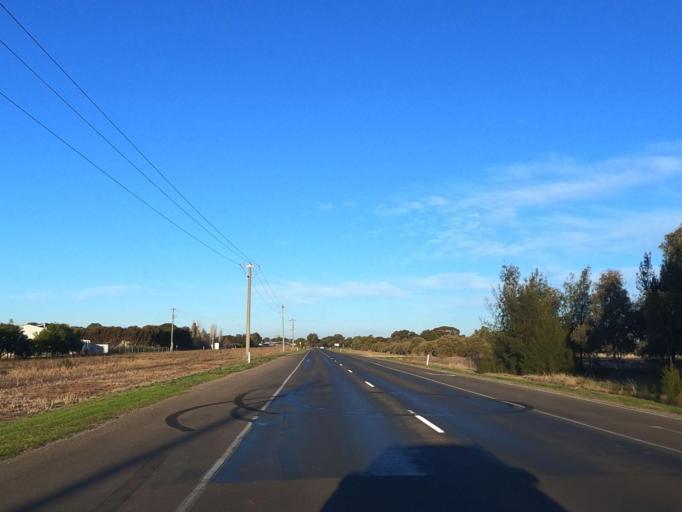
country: AU
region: Victoria
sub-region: Swan Hill
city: Swan Hill
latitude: -35.3358
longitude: 143.5341
